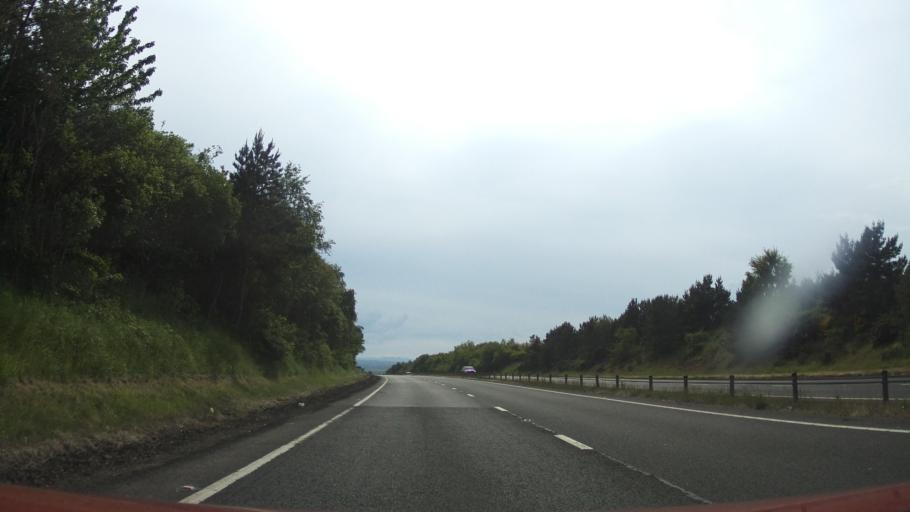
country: GB
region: Scotland
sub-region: East Lothian
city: East Linton
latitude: 55.9793
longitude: -2.6902
